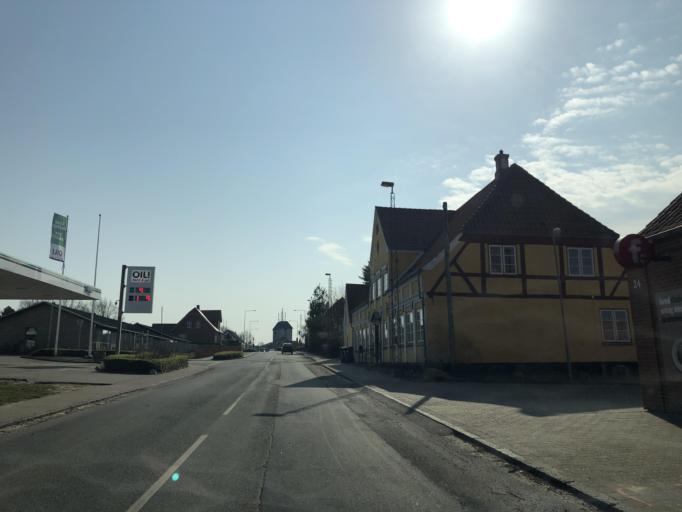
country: DK
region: South Denmark
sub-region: Sonderborg Kommune
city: Nordborg
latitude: 55.0559
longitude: 9.7486
